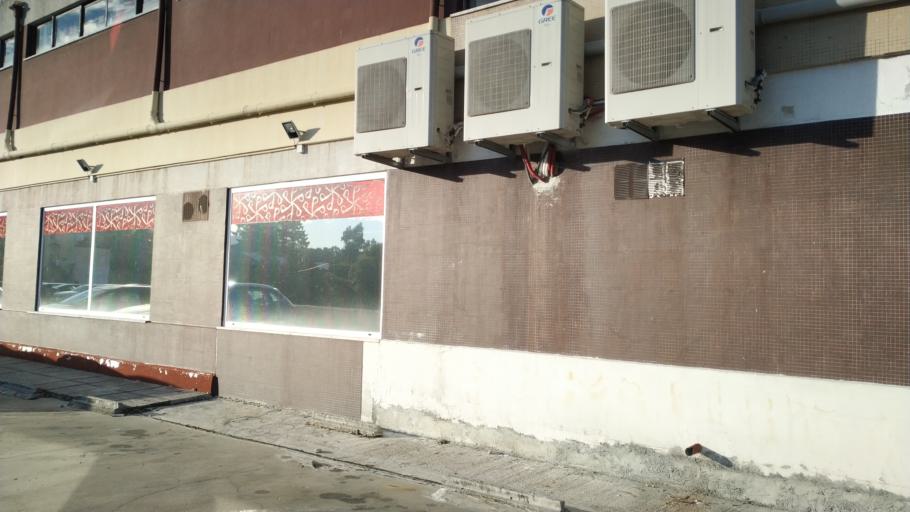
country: PT
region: Vila Real
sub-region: Vila Real
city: Vila Real
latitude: 41.2947
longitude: -7.7439
